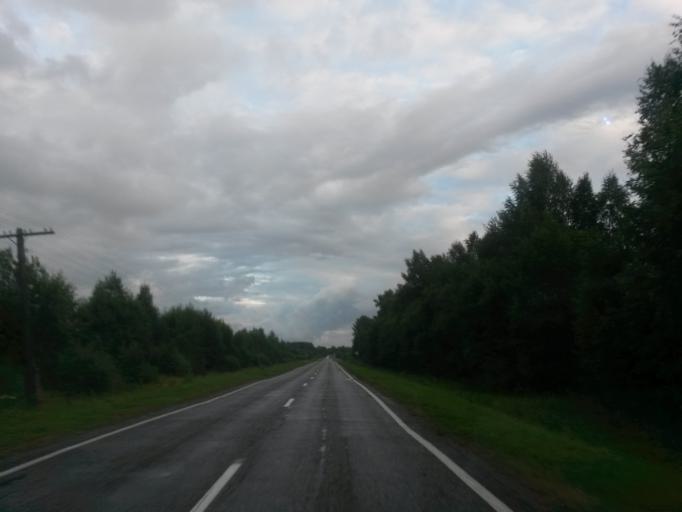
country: RU
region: Jaroslavl
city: Tutayev
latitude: 57.9077
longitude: 39.5202
